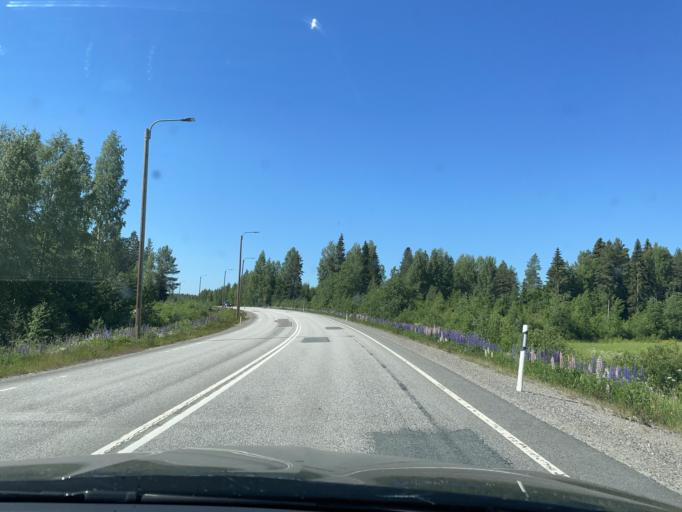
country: FI
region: Central Finland
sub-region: Saarijaervi-Viitasaari
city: Viitasaari
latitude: 63.1453
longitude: 25.8069
